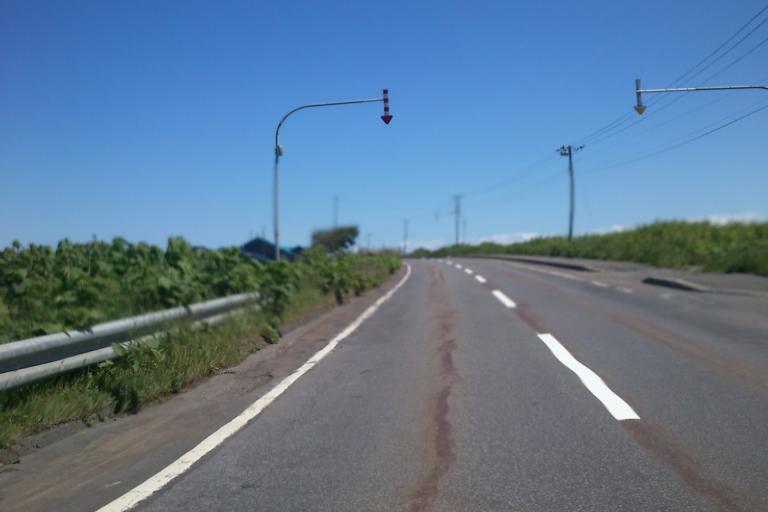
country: JP
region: Hokkaido
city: Rumoi
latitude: 43.8459
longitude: 141.5032
